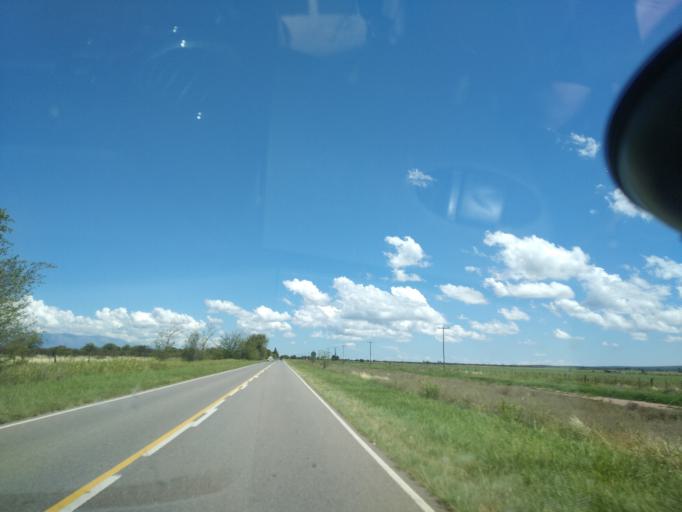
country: AR
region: Cordoba
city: Villa Cura Brochero
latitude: -31.5719
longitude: -65.1122
